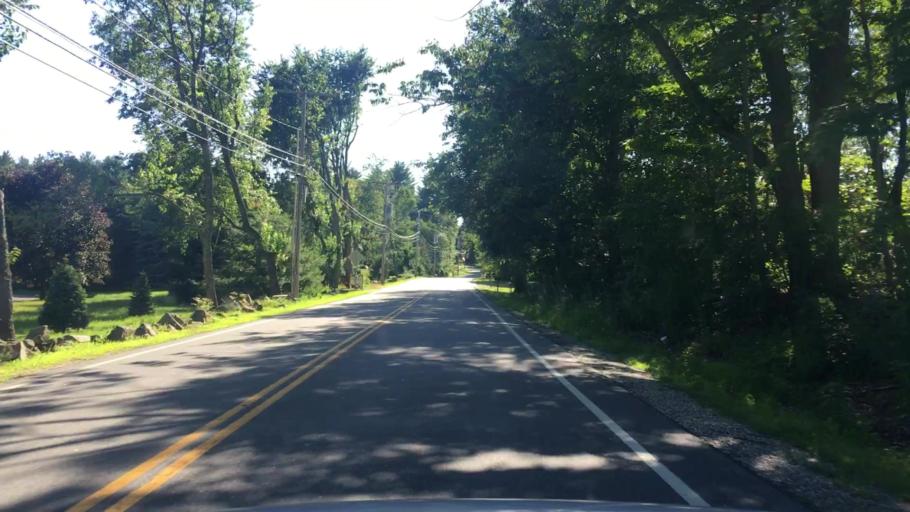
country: US
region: New Hampshire
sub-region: Rockingham County
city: Brentwood
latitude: 42.9861
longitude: -71.0590
